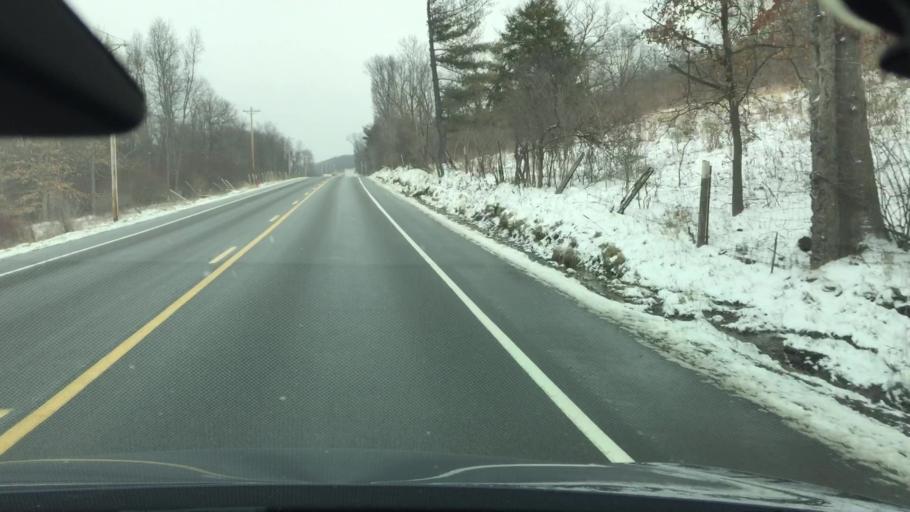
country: US
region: Pennsylvania
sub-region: Jefferson County
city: Brookville
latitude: 41.0576
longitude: -79.2483
